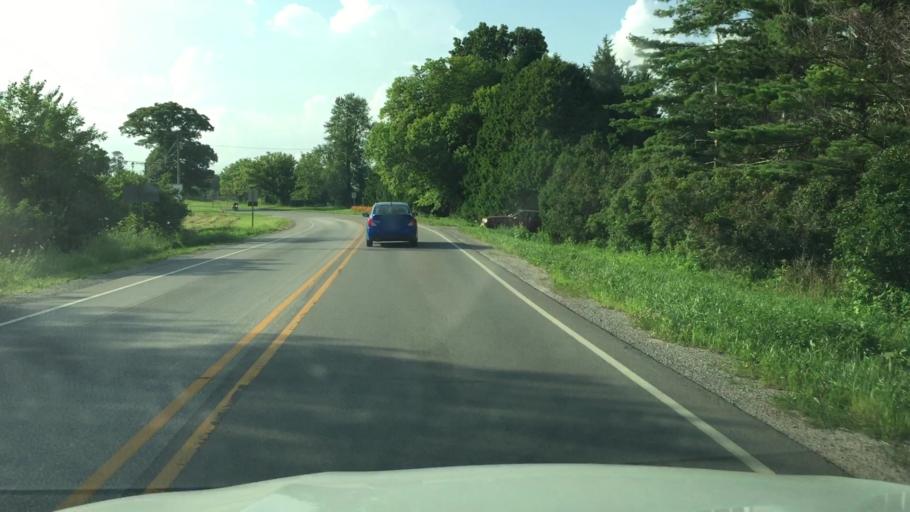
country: US
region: Iowa
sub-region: Linn County
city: Ely
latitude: 41.8354
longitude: -91.6362
